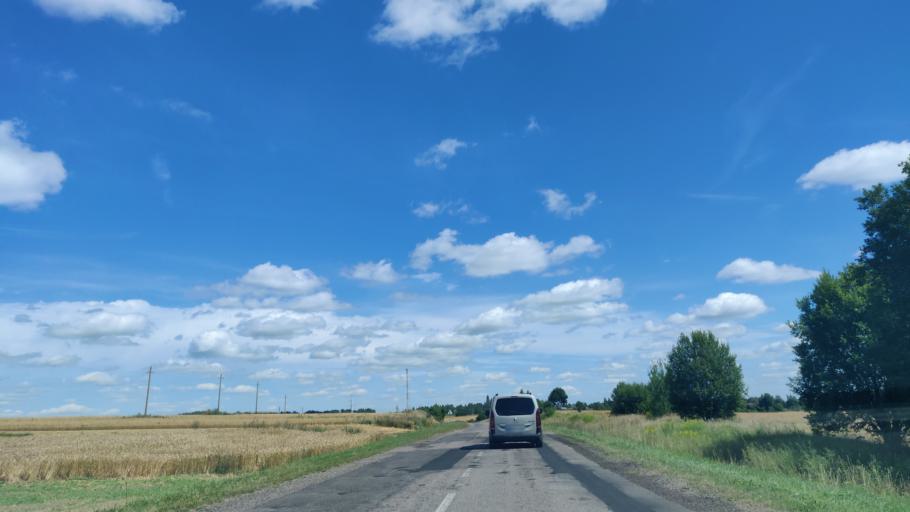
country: LT
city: Salcininkai
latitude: 54.4567
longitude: 25.4830
